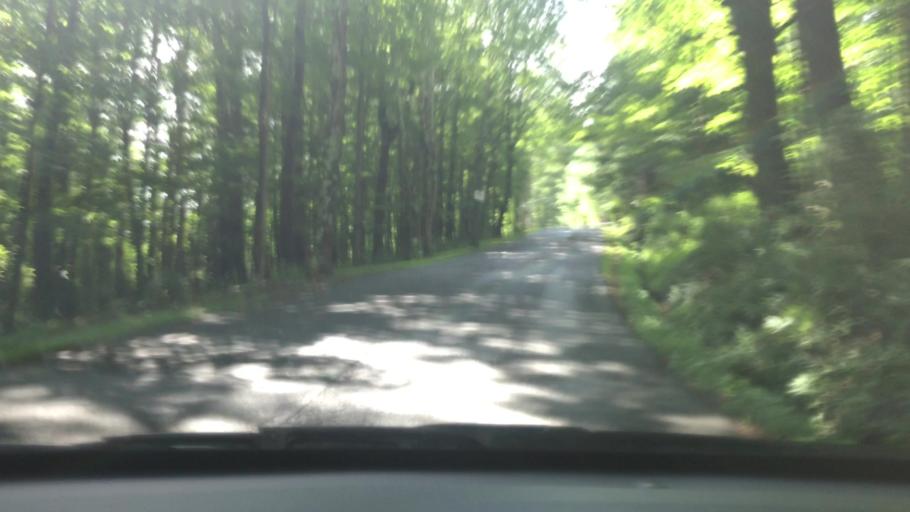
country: US
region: New York
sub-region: Ulster County
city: Shokan
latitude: 41.9636
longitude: -74.2835
